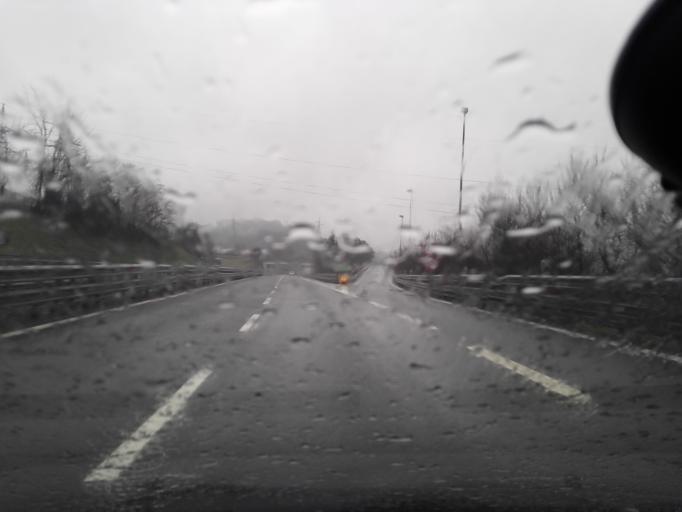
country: IT
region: Piedmont
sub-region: Provincia di Alessandria
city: Vignole Borbera
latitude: 44.7033
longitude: 8.8848
